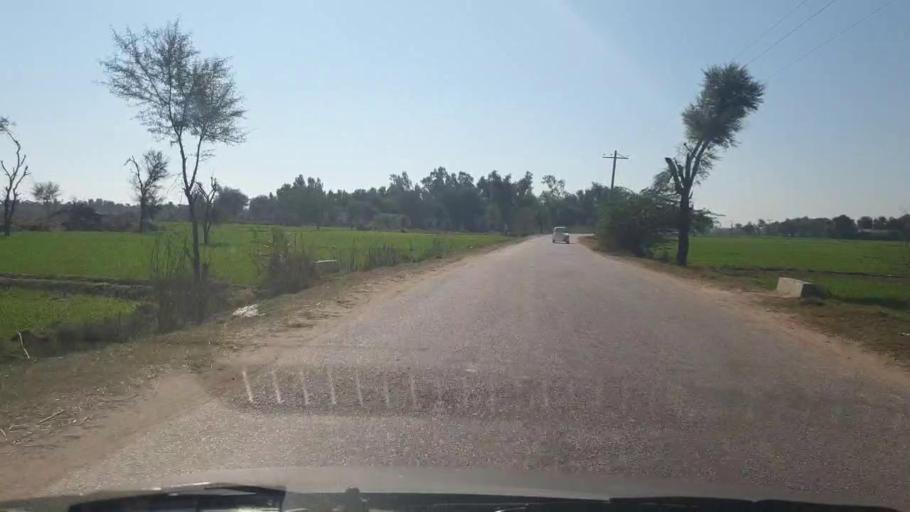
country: PK
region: Sindh
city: Bozdar
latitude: 27.0884
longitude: 68.6238
